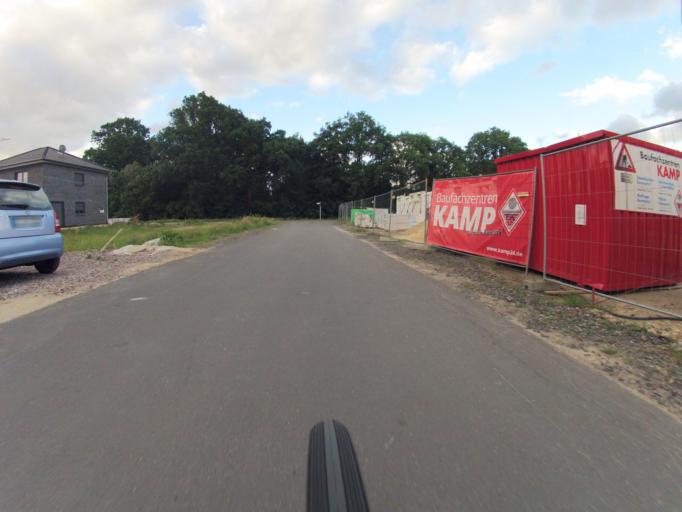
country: DE
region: North Rhine-Westphalia
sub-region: Regierungsbezirk Munster
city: Birgte
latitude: 52.2940
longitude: 7.6469
